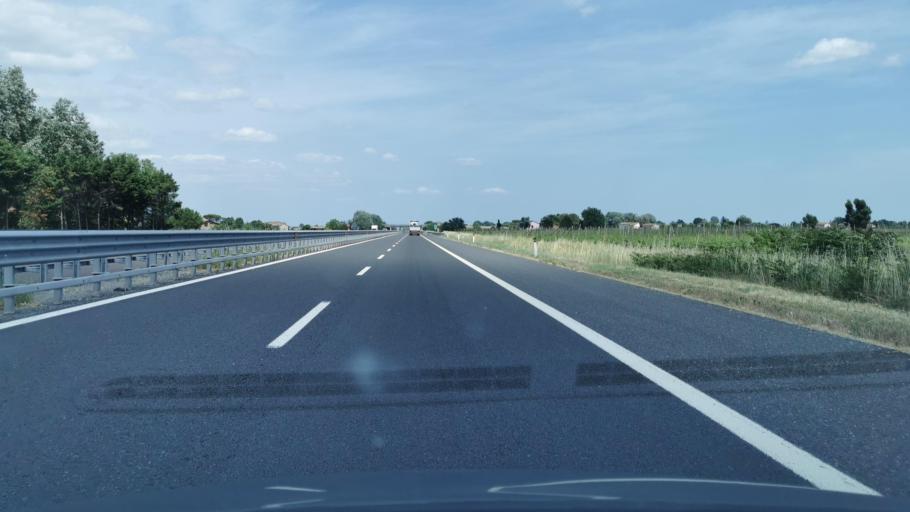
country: IT
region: Emilia-Romagna
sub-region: Provincia di Ravenna
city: Barbiano
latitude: 44.3801
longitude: 11.8852
